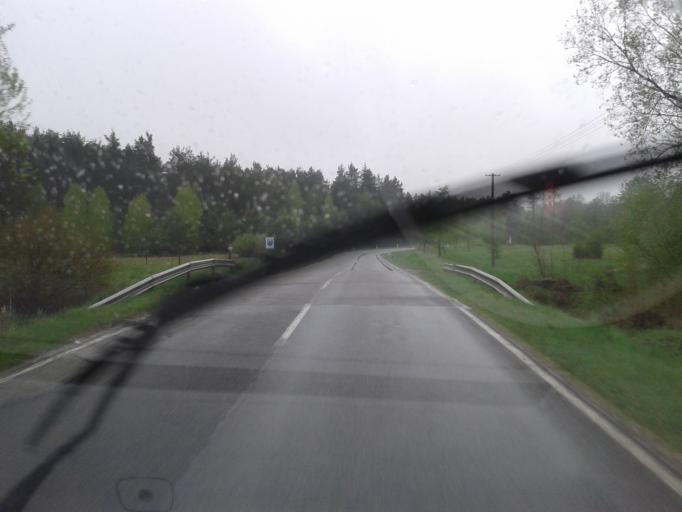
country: PL
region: Subcarpathian Voivodeship
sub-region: Powiat lubaczowski
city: Narol
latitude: 50.3085
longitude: 23.2374
